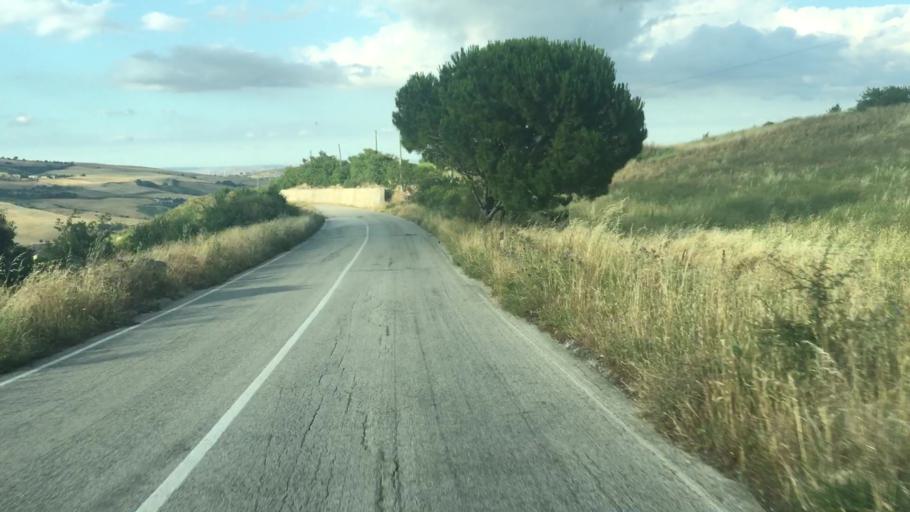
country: IT
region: Basilicate
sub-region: Provincia di Potenza
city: Tolve
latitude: 40.6951
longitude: 15.9916
